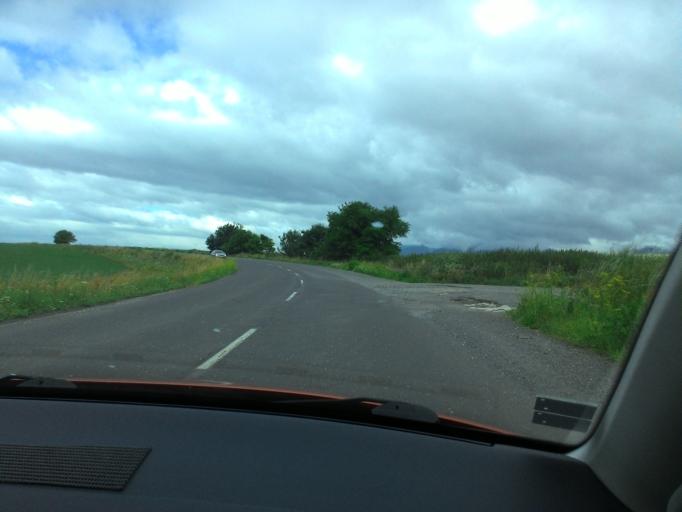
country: SK
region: Zilinsky
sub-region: Okres Liptovsky Mikulas
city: Hybe
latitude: 49.0571
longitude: 19.8720
